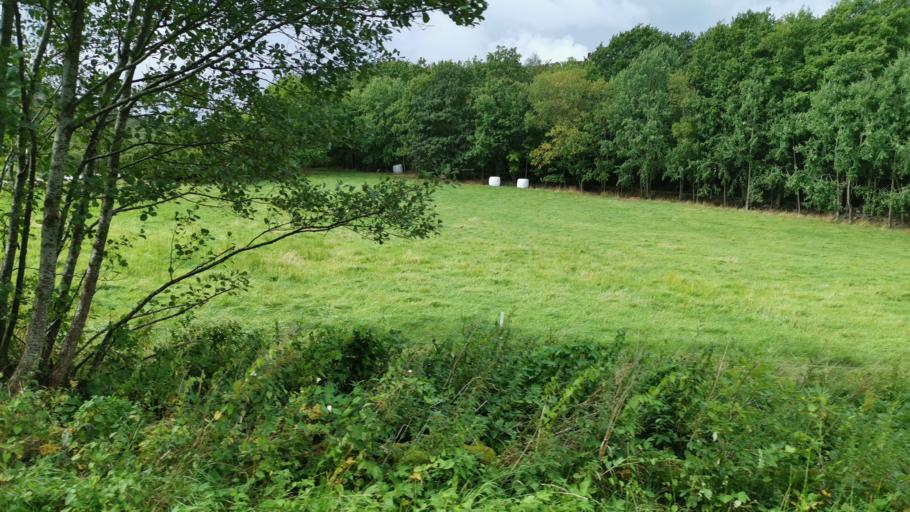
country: SE
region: Vaestra Goetaland
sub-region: Tjorns Kommun
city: Skaerhamn
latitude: 58.0492
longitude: 11.5798
